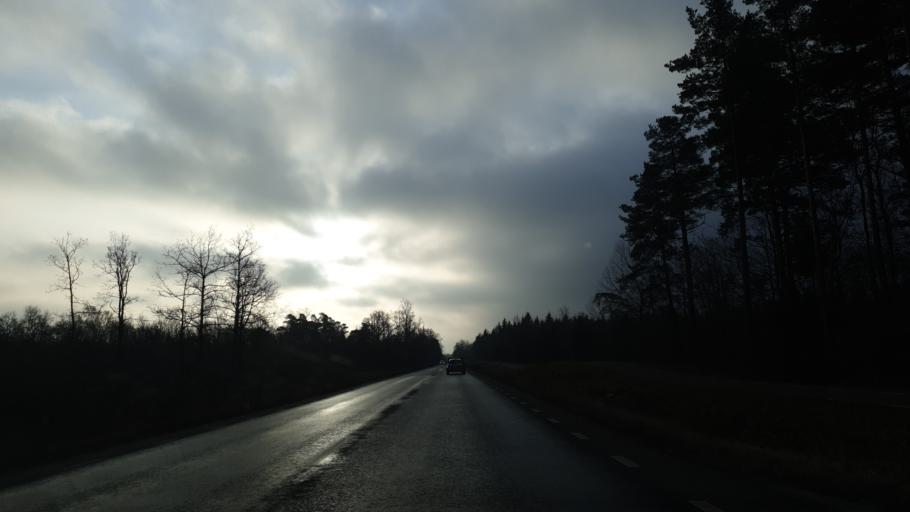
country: SE
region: Blekinge
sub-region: Karlshamns Kommun
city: Morrum
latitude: 56.1442
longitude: 14.6693
